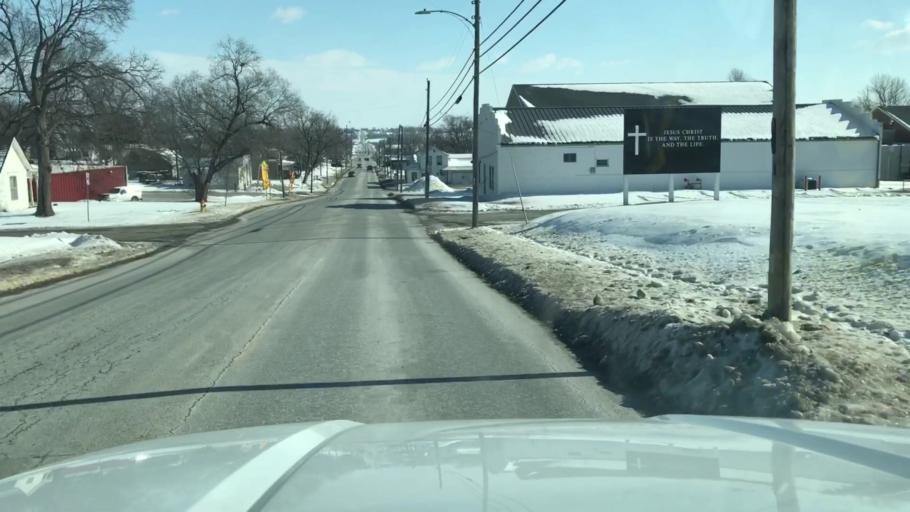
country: US
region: Missouri
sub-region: Nodaway County
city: Maryville
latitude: 40.3454
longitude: -94.8615
